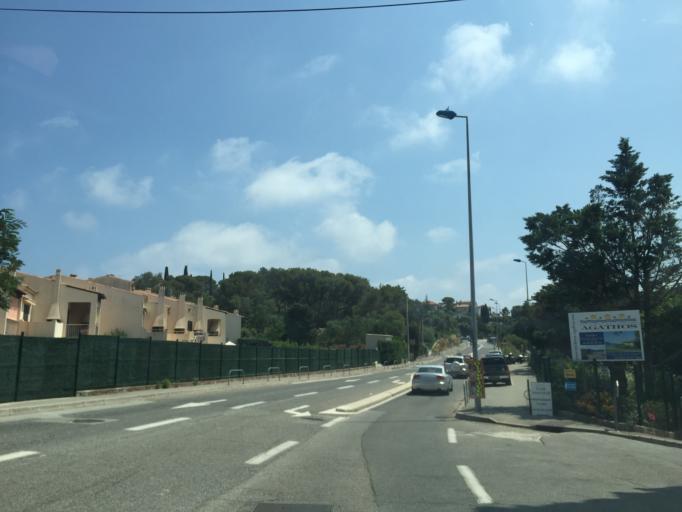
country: FR
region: Provence-Alpes-Cote d'Azur
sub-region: Departement du Var
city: Saint-Raphael
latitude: 43.4303
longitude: 6.8709
